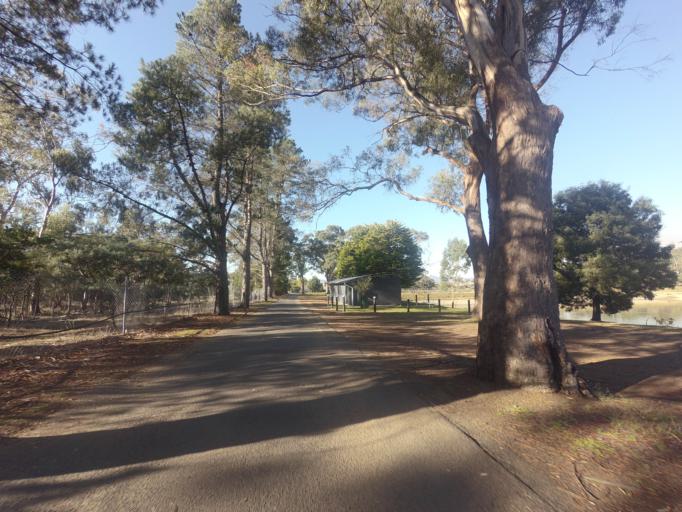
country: AU
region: Tasmania
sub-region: Glenorchy
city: Glenorchy
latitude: -42.8496
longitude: 147.2515
